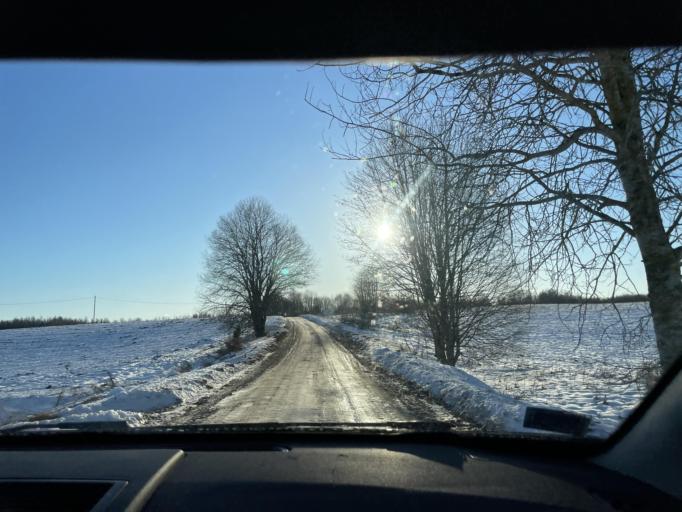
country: LV
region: Ludzas Rajons
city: Ludza
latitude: 56.4568
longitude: 27.6349
